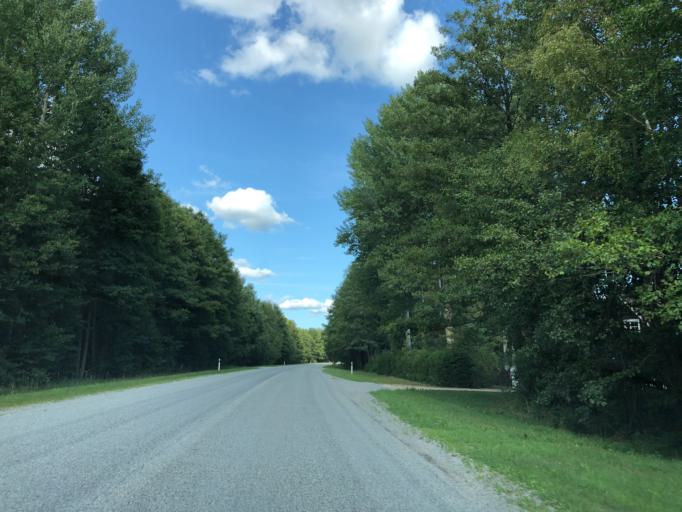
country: EE
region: Hiiumaa
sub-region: Kaerdla linn
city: Kardla
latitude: 58.8205
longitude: 22.7414
